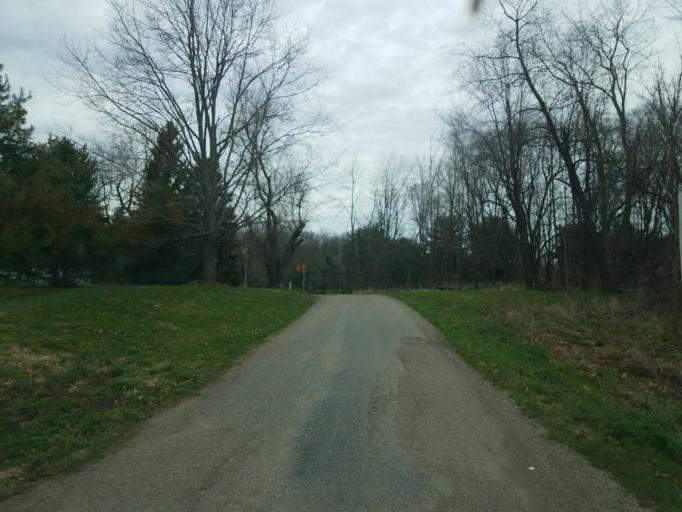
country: US
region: Ohio
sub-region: Knox County
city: Fredericktown
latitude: 40.4697
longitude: -82.5743
